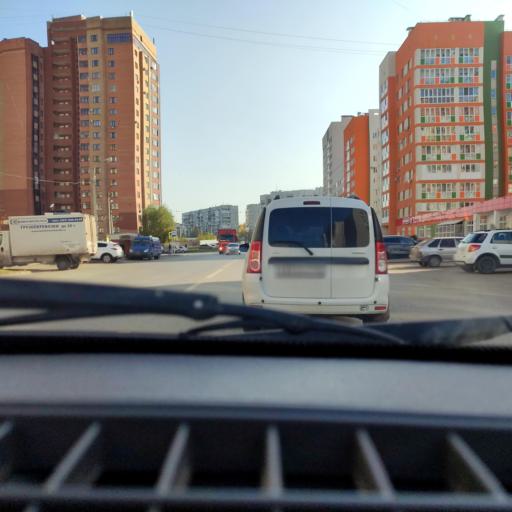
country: RU
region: Bashkortostan
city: Mikhaylovka
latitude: 54.7129
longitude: 55.8351
